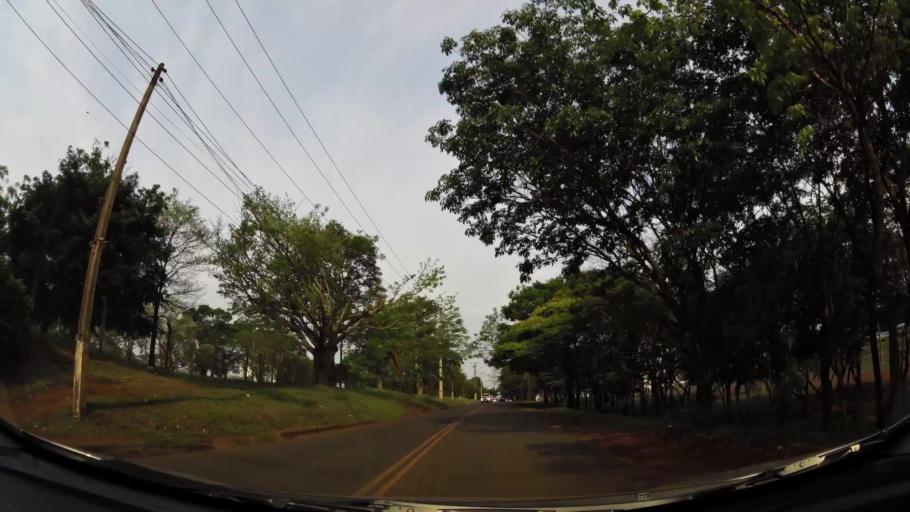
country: PY
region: Alto Parana
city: Ciudad del Este
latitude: -25.4968
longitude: -54.6691
